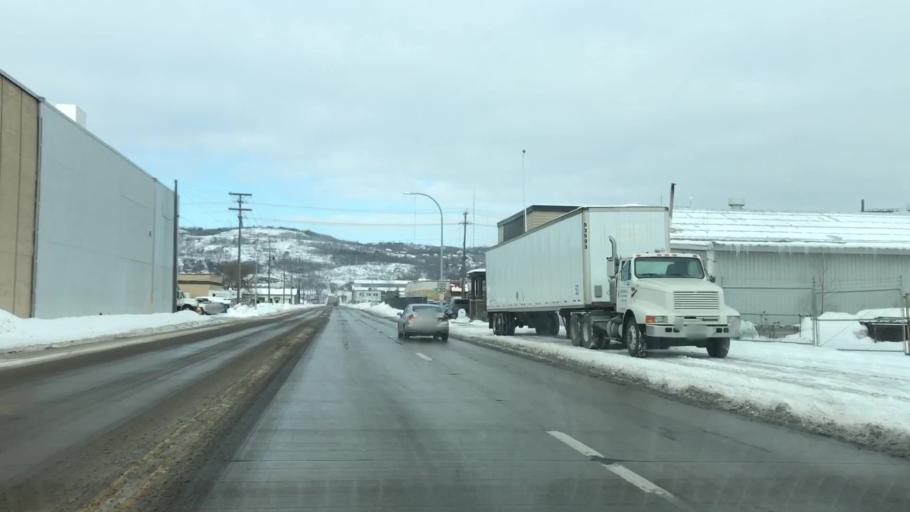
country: US
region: Minnesota
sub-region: Saint Louis County
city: Duluth
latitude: 46.7608
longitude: -92.1100
